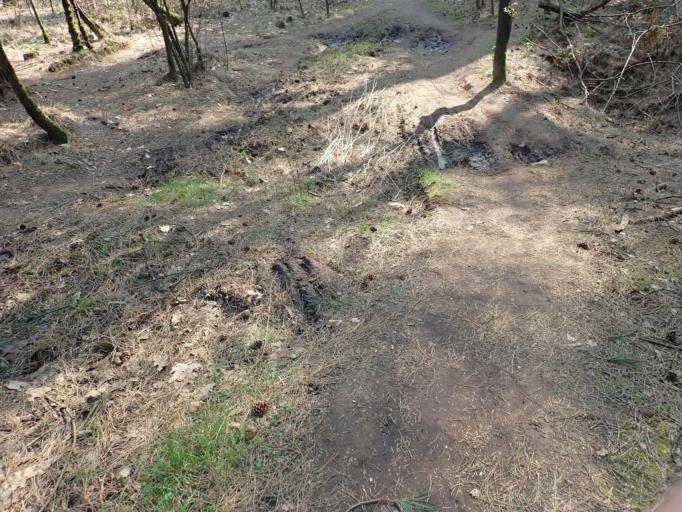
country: BE
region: Flanders
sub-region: Provincie Antwerpen
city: Essen
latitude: 51.4727
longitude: 4.5321
